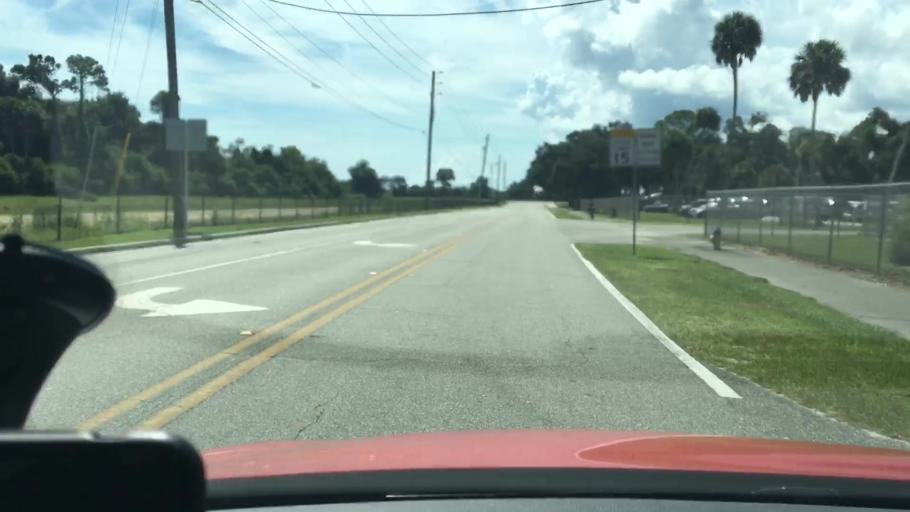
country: US
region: Florida
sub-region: Volusia County
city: New Smyrna Beach
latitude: 29.0053
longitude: -80.9228
